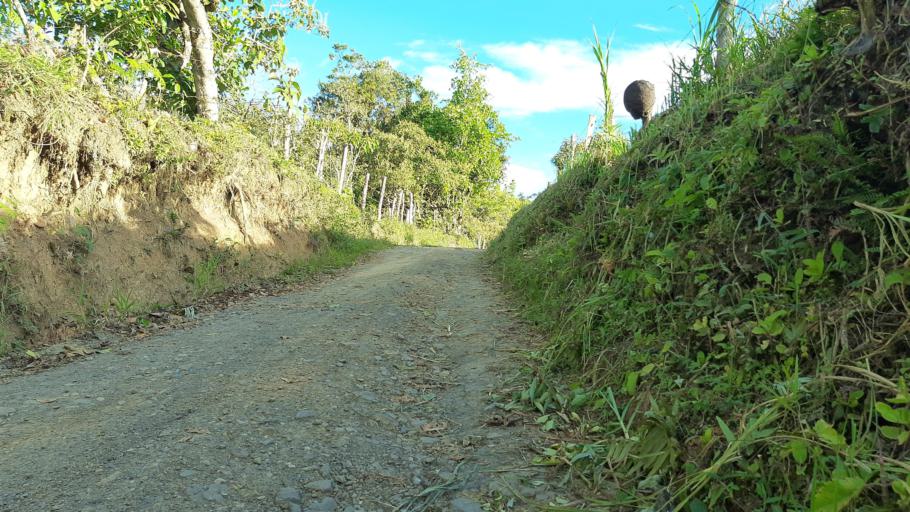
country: CO
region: Boyaca
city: Garagoa
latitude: 5.0703
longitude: -73.3768
